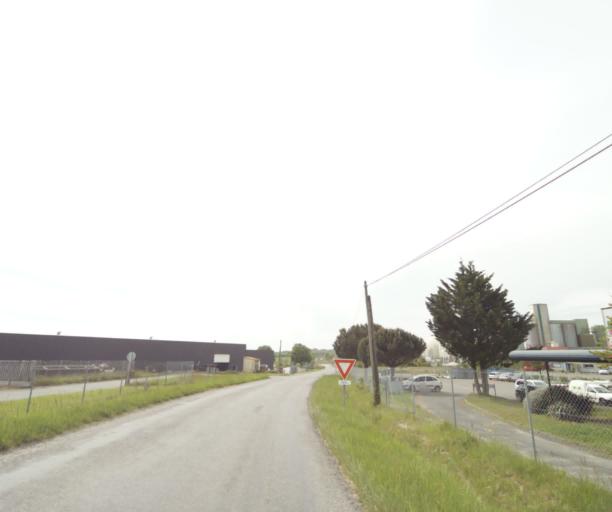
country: FR
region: Poitou-Charentes
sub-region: Departement de la Charente-Maritime
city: Saintes
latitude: 45.7173
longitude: -0.6523
